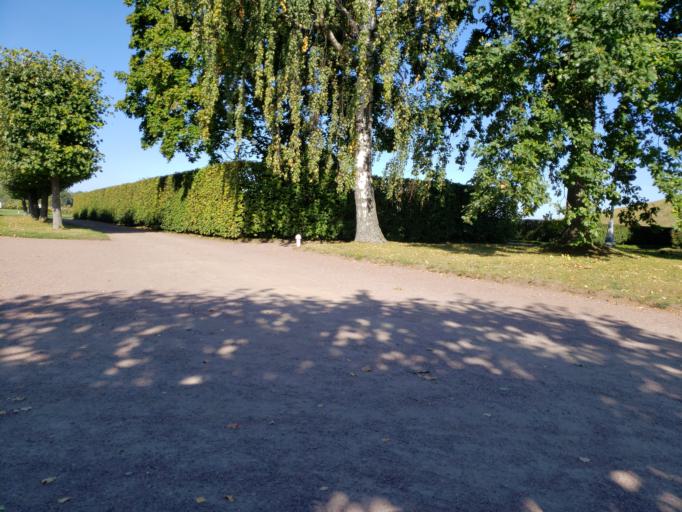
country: RU
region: St.-Petersburg
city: Peterhof
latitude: 59.8890
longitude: 29.8957
